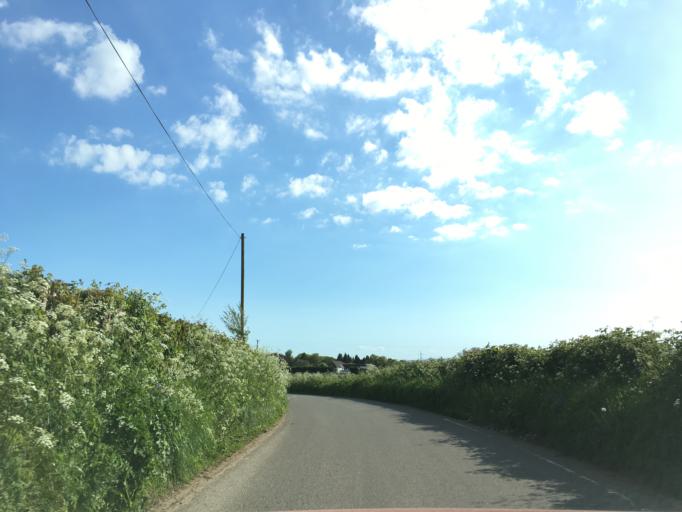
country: GB
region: Wales
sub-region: Newport
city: Marshfield
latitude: 51.5419
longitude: -3.1008
